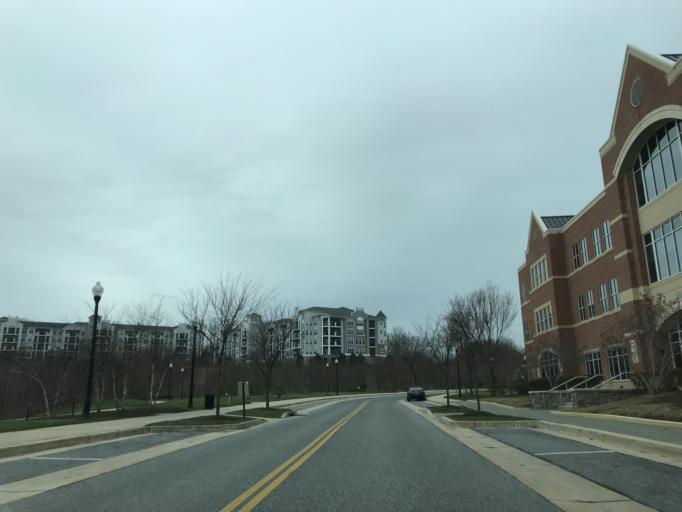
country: US
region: Maryland
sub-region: Baltimore County
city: Pikesville
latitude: 39.3841
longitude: -76.6941
